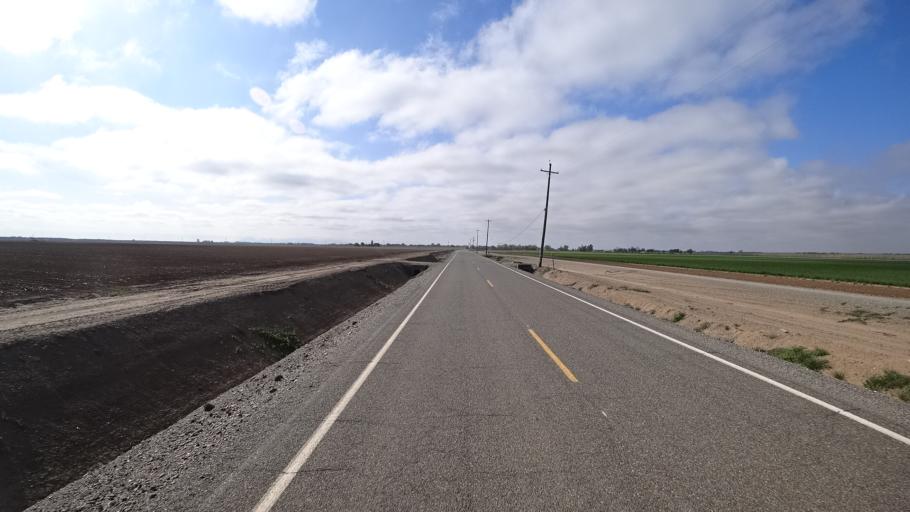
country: US
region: California
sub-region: Colusa County
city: Colusa
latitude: 39.4388
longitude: -121.9672
